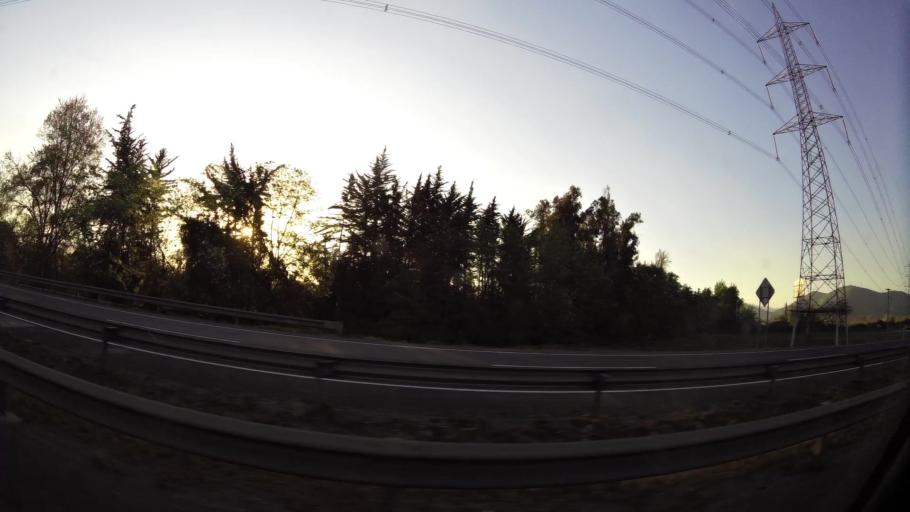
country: CL
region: Santiago Metropolitan
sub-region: Provincia de Talagante
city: Penaflor
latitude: -33.5692
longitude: -70.8480
